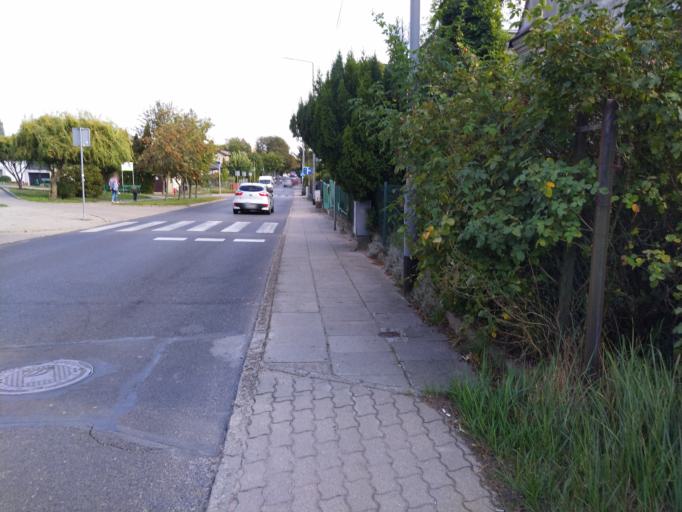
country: PL
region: West Pomeranian Voivodeship
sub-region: Szczecin
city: Szczecin
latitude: 53.4638
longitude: 14.5662
